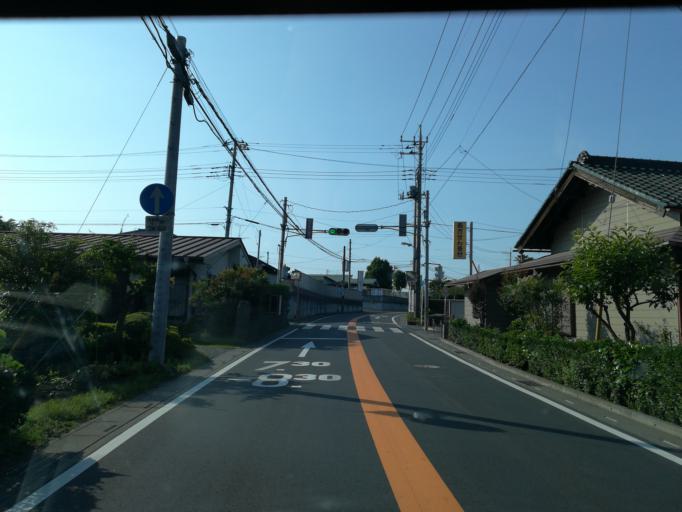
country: JP
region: Saitama
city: Sayama
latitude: 35.7936
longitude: 139.4072
